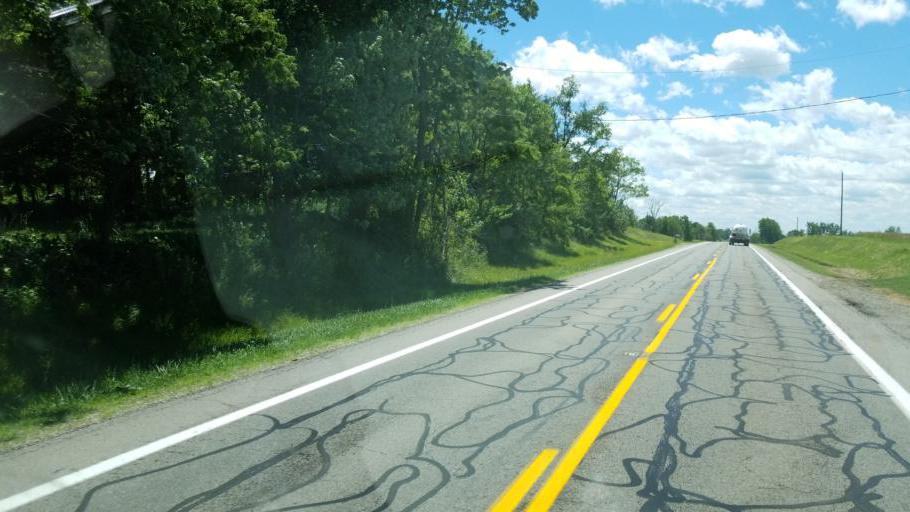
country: US
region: Ohio
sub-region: Crawford County
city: Galion
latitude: 40.6584
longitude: -82.8218
